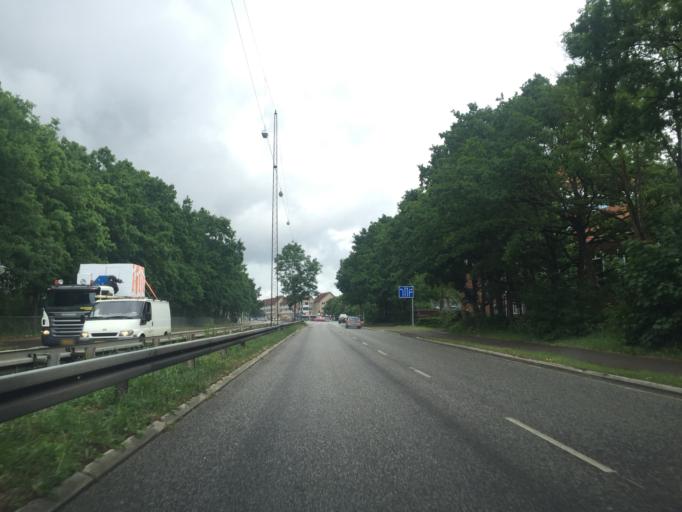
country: DK
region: Capital Region
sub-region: Rodovre Kommune
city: Rodovre
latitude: 55.6687
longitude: 12.4562
